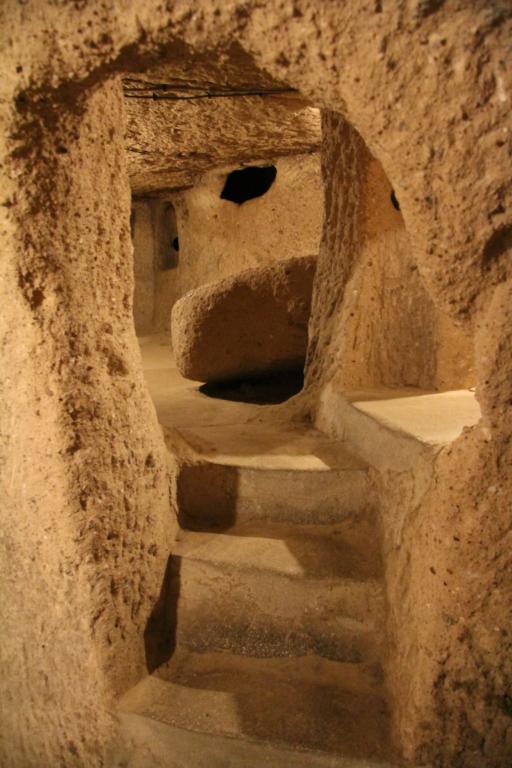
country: TR
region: Nevsehir
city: Derinkuyu
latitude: 38.4601
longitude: 34.7519
